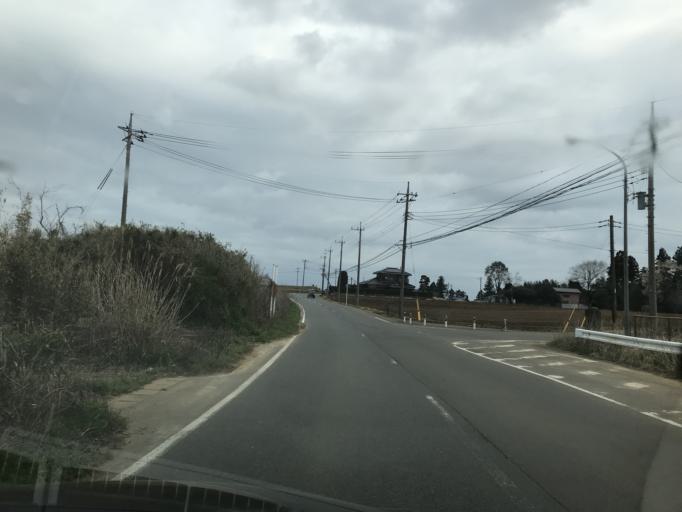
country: JP
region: Chiba
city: Sawara
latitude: 35.8349
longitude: 140.4948
